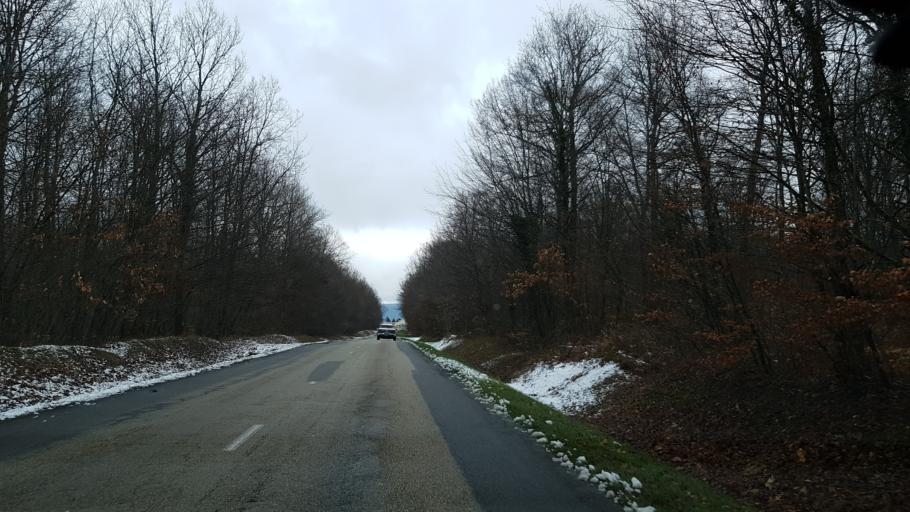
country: FR
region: Rhone-Alpes
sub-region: Departement de l'Ain
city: Bourg-en-Bresse
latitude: 46.1759
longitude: 5.2492
